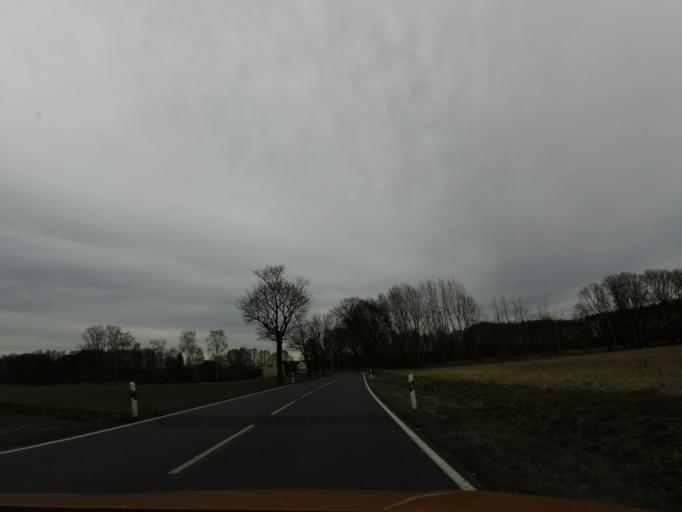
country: DE
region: Brandenburg
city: Belzig
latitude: 52.1519
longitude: 12.6494
